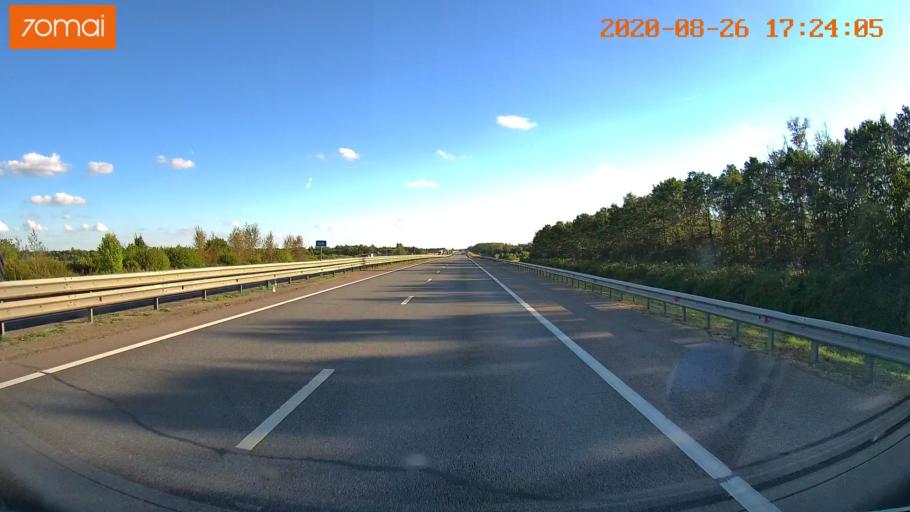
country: RU
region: Tula
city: Volovo
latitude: 53.5239
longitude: 38.1172
